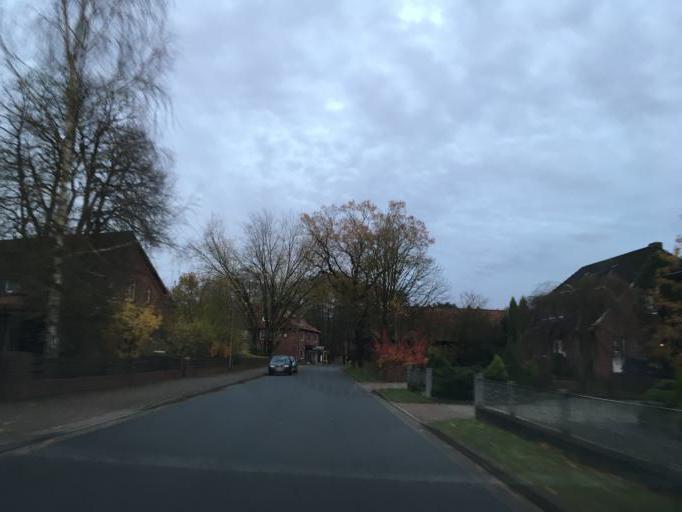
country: DE
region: Lower Saxony
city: Bispingen
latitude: 53.0964
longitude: 10.0241
